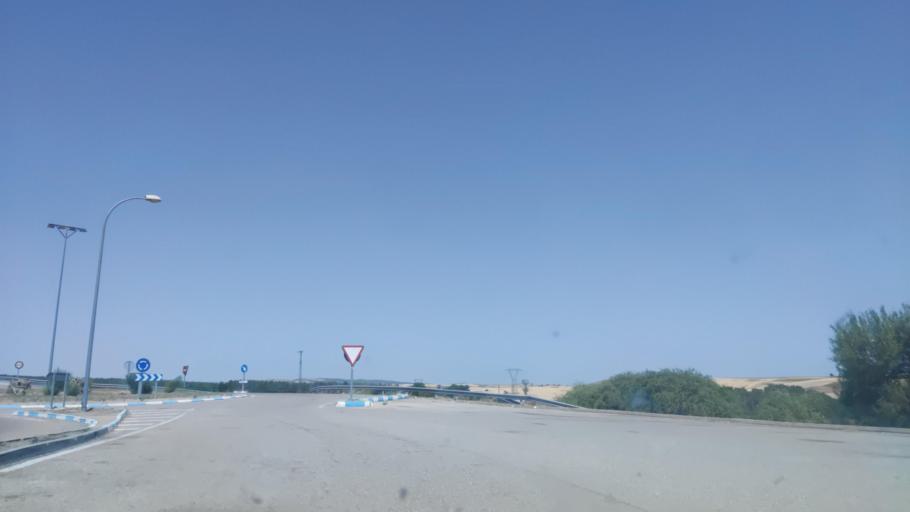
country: ES
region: Castille-La Mancha
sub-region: Provincia de Cuenca
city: Montalbo
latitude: 39.9044
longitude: -2.7145
